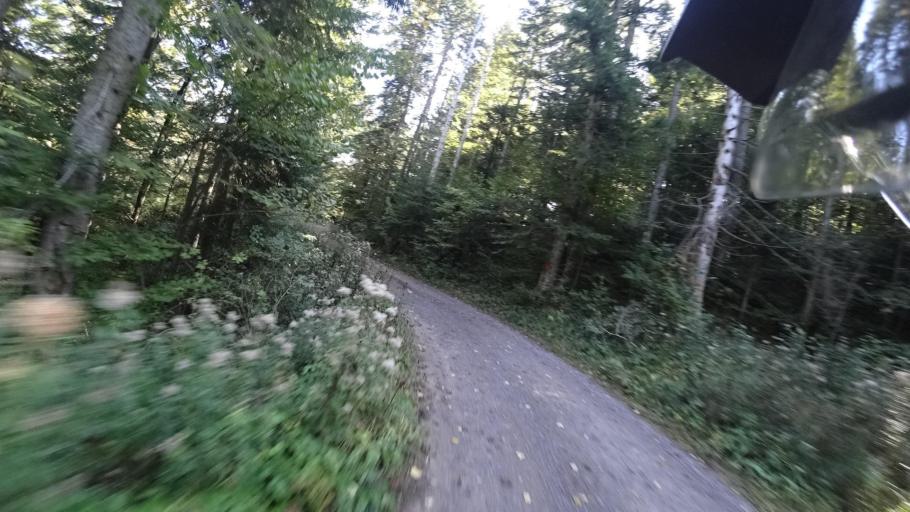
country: HR
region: Primorsko-Goranska
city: Vrbovsko
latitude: 45.2612
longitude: 15.1048
